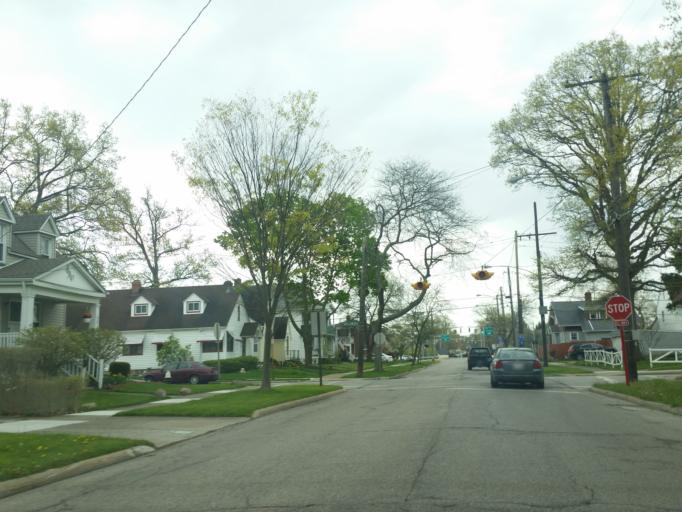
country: US
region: Ohio
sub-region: Cuyahoga County
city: Lakewood
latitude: 41.4714
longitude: -81.8005
